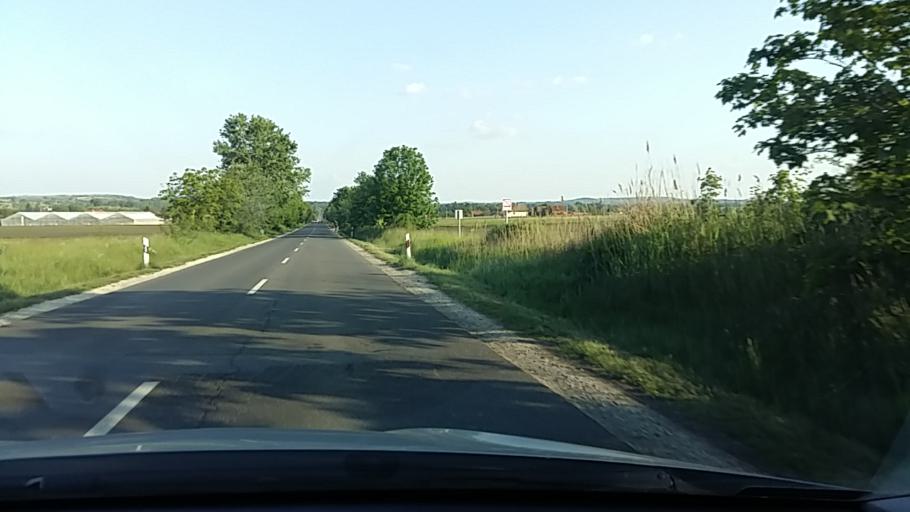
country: HU
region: Pest
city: Szod
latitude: 47.7275
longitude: 19.2260
